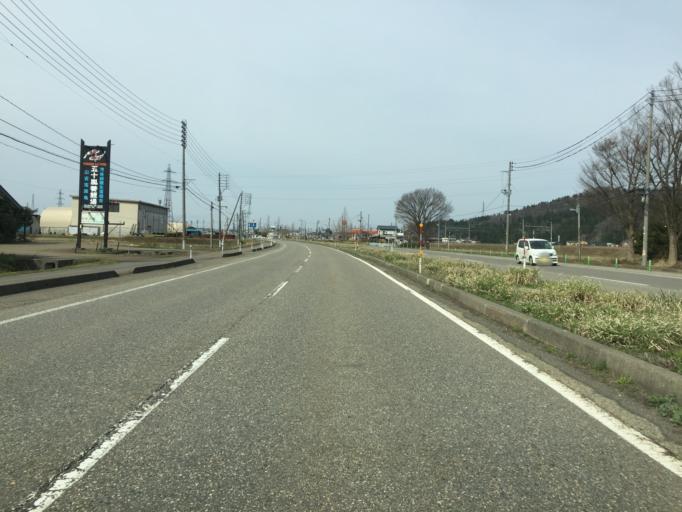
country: JP
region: Niigata
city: Ojiya
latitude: 37.3609
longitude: 138.8333
